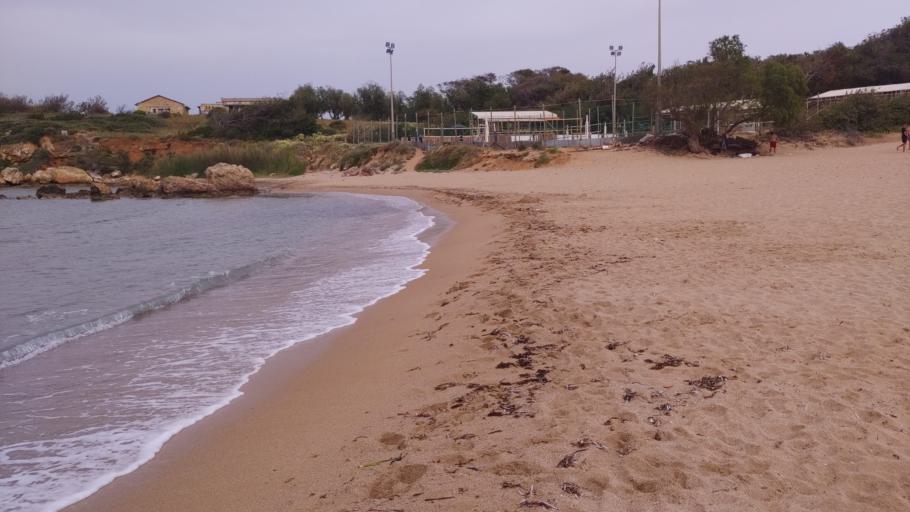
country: GR
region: Crete
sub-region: Nomos Chanias
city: Daratsos
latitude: 35.5141
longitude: 23.9786
